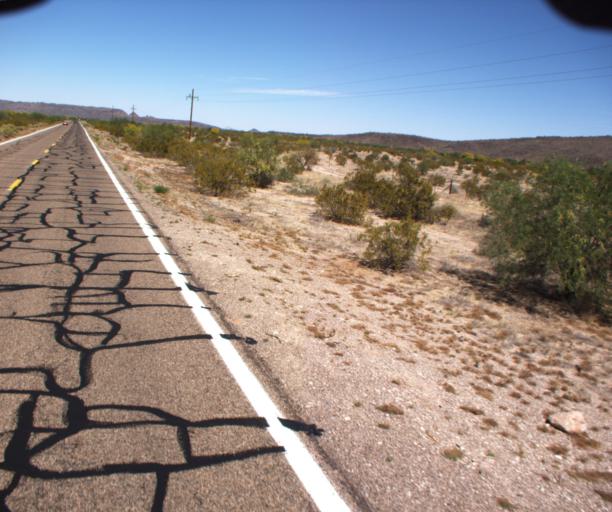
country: US
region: Arizona
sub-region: Pima County
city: Ajo
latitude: 32.4814
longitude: -112.8791
